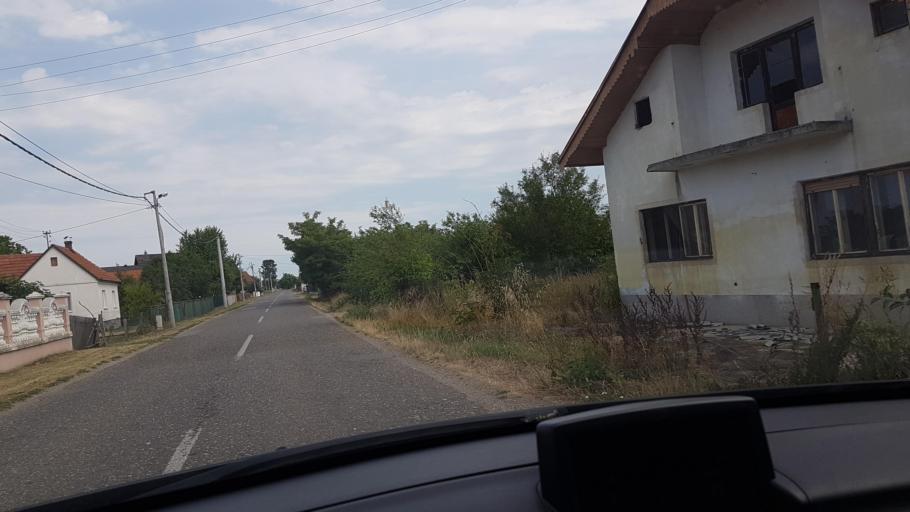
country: BA
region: Republika Srpska
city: Dvorovi
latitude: 44.8157
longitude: 19.2175
